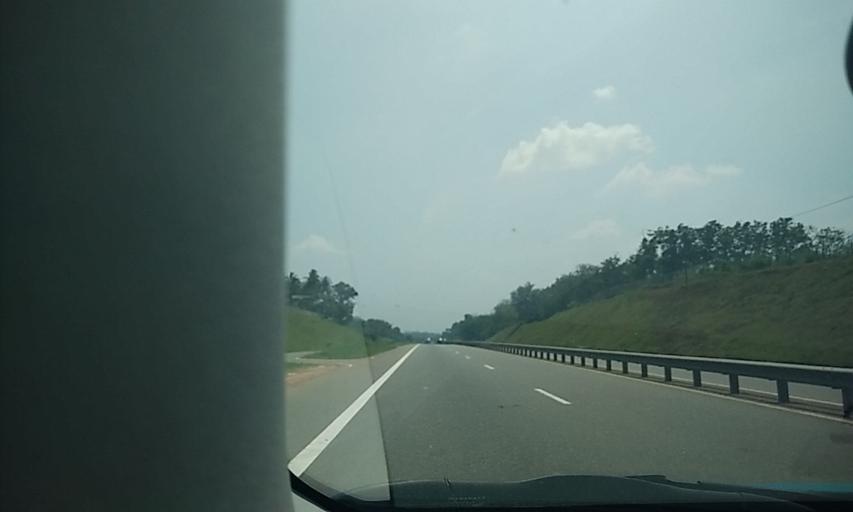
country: LK
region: Western
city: Homagama
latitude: 6.7647
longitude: 79.9862
